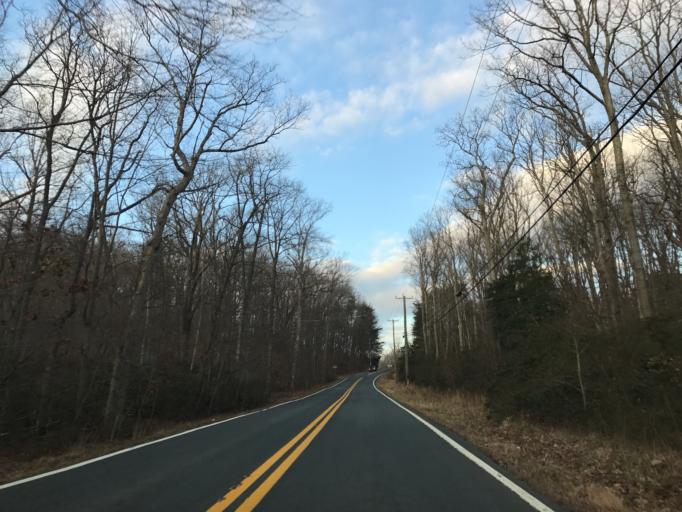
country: US
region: Maryland
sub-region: Cecil County
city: Charlestown
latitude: 39.5044
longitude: -75.9596
